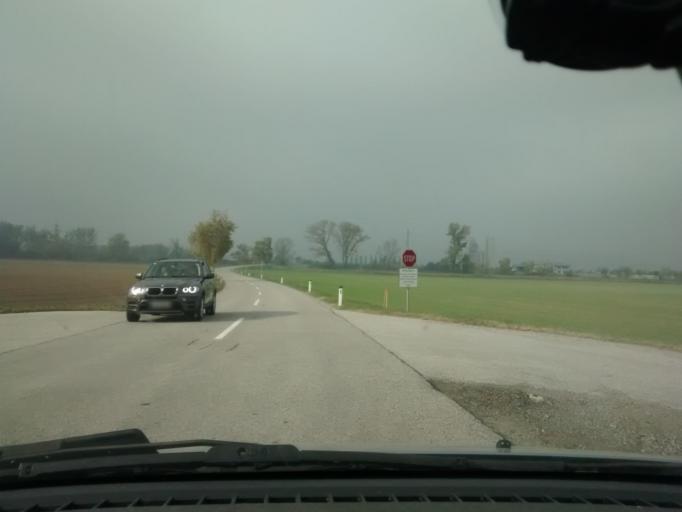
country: AT
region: Lower Austria
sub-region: Politischer Bezirk Modling
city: Guntramsdorf
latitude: 48.0393
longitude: 16.3380
